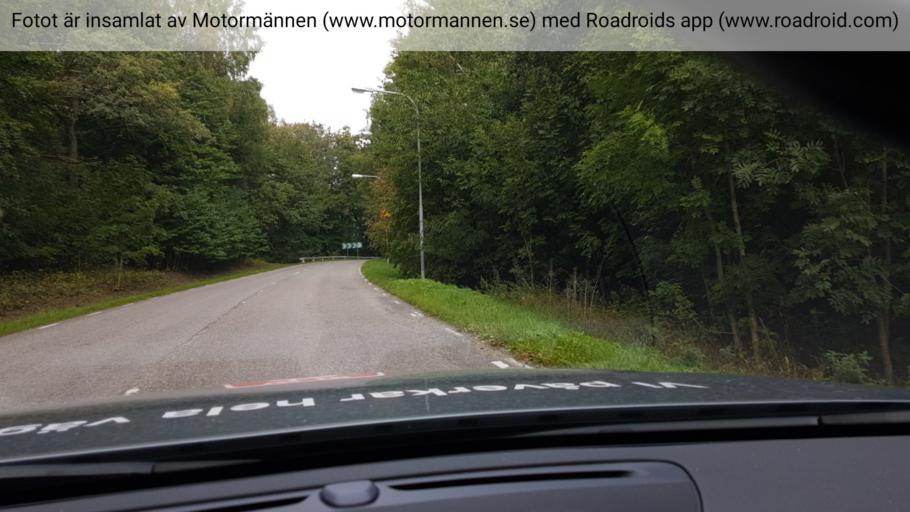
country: SE
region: Stockholm
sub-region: Stockholms Kommun
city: OEstermalm
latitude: 59.3560
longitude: 18.0836
